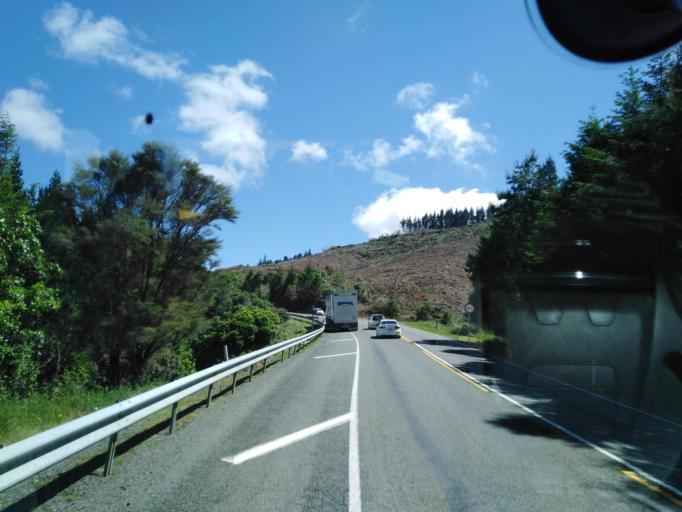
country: NZ
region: Nelson
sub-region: Nelson City
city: Nelson
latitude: -41.1949
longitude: 173.5580
